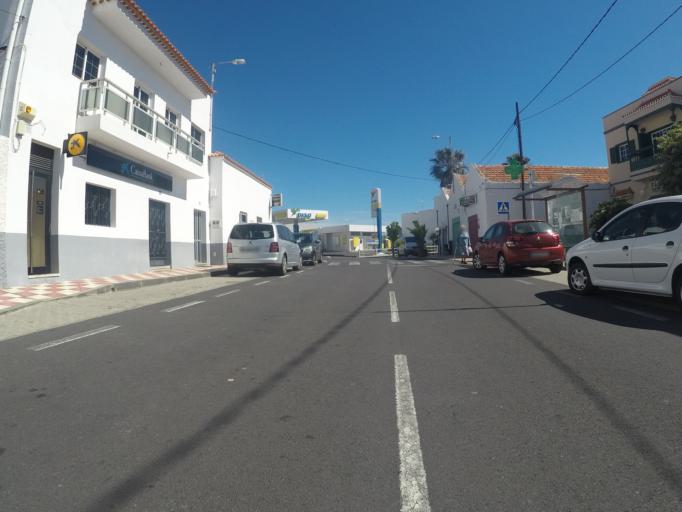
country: ES
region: Canary Islands
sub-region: Provincia de Santa Cruz de Tenerife
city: Lomo de Arico
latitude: 28.1821
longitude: -16.4802
